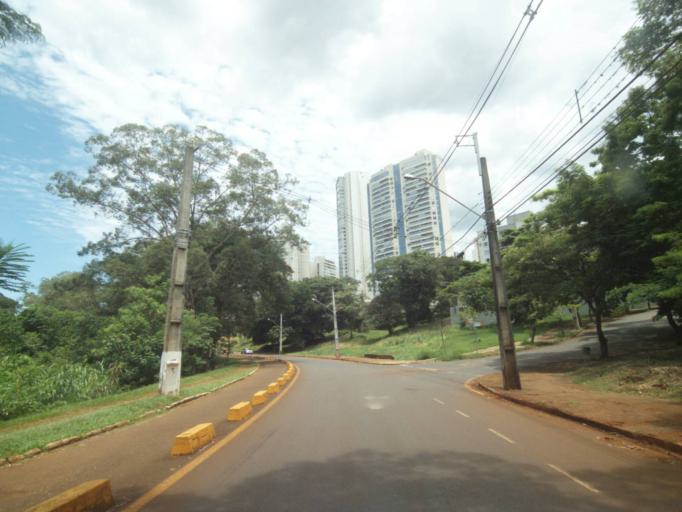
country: BR
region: Parana
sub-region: Londrina
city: Londrina
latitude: -23.3242
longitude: -51.1811
